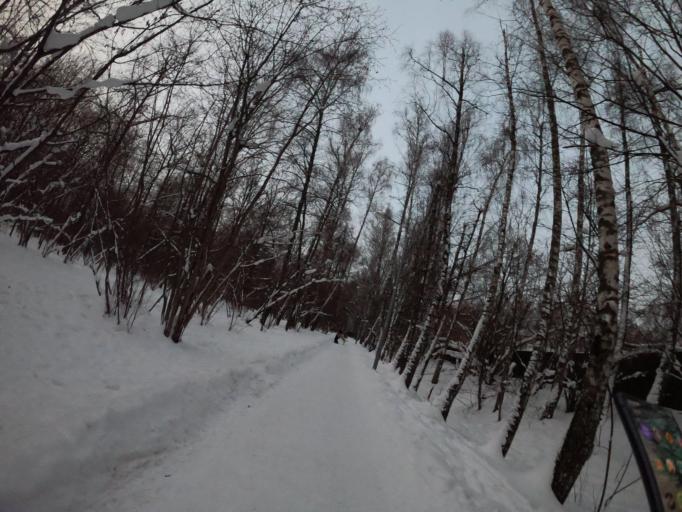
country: RU
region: Moskovskaya
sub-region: Podol'skiy Rayon
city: Podol'sk
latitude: 55.4162
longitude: 37.5261
